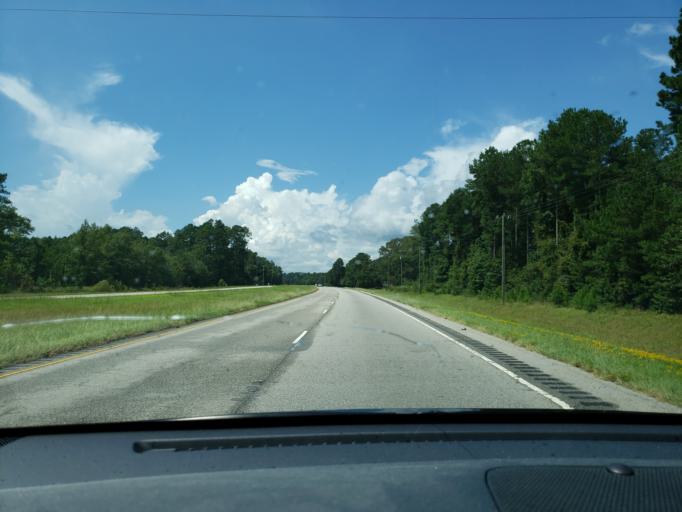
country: US
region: North Carolina
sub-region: Bladen County
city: Elizabethtown
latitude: 34.6437
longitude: -78.6799
